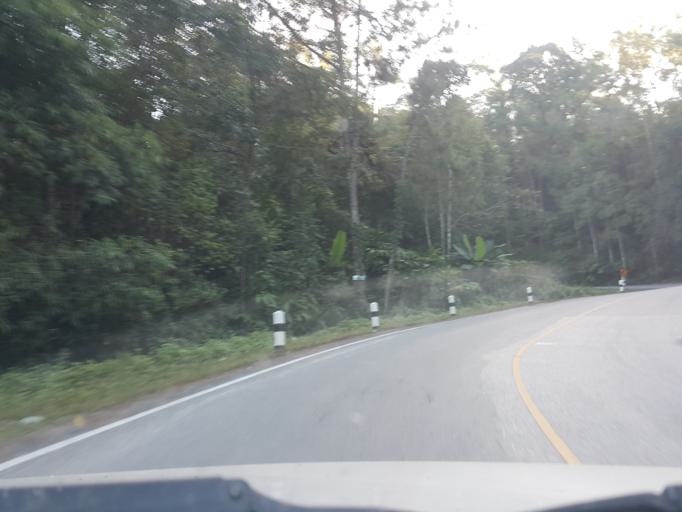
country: TH
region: Mae Hong Son
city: Mae Hi
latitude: 19.2726
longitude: 98.5780
